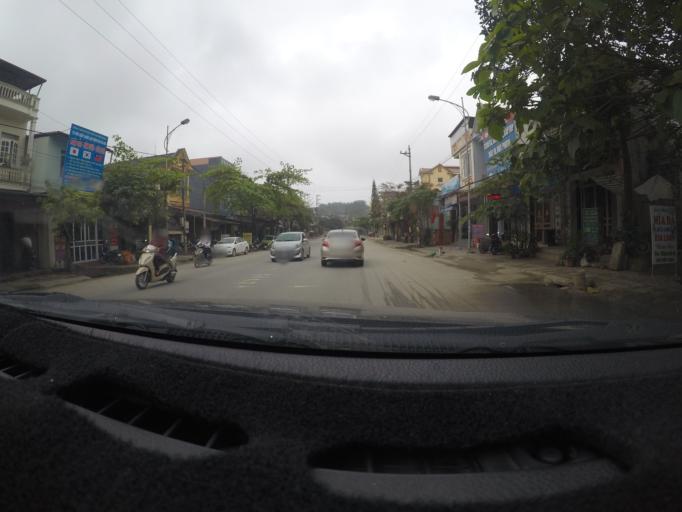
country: VN
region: Yen Bai
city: Yen Bai
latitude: 21.7327
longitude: 104.9580
